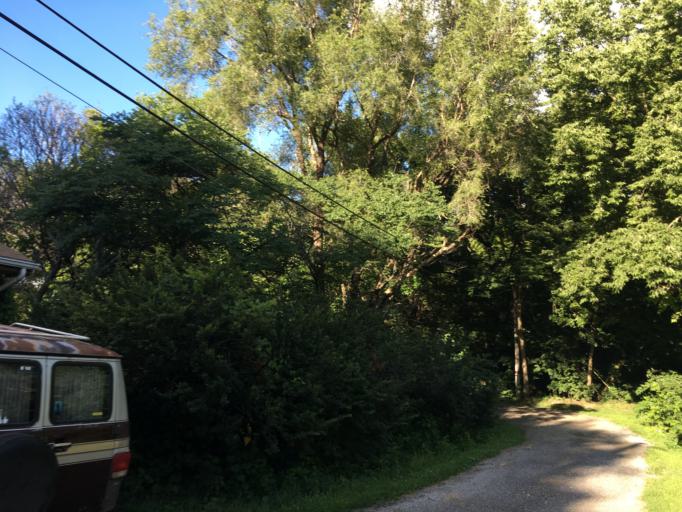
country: US
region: Nebraska
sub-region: Sarpy County
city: La Vista
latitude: 41.1872
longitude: -95.9822
